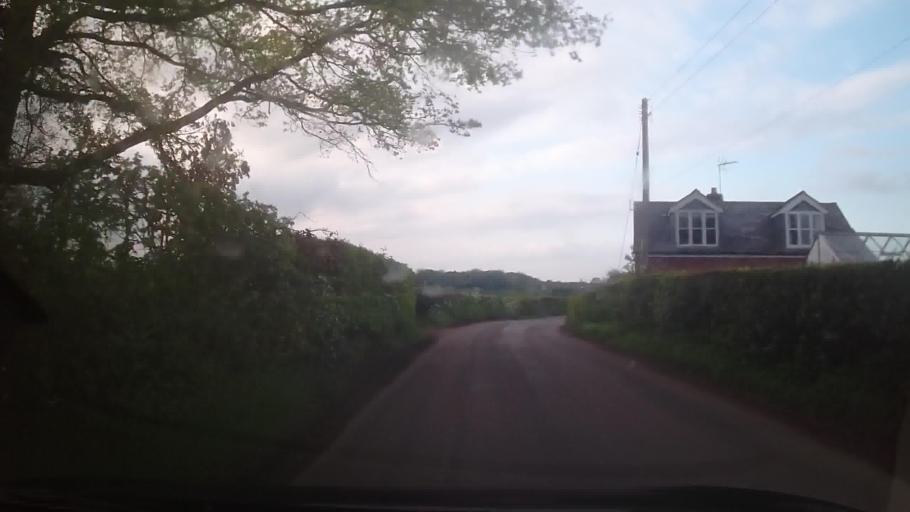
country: GB
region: England
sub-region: Shropshire
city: Ellesmere
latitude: 52.9419
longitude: -2.8730
